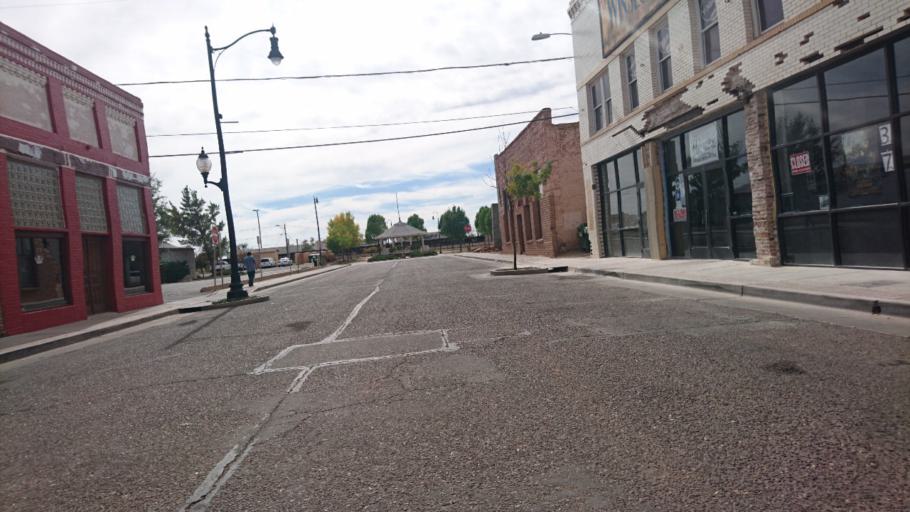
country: US
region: Arizona
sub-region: Navajo County
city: Winslow
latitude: 35.0232
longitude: -110.6981
